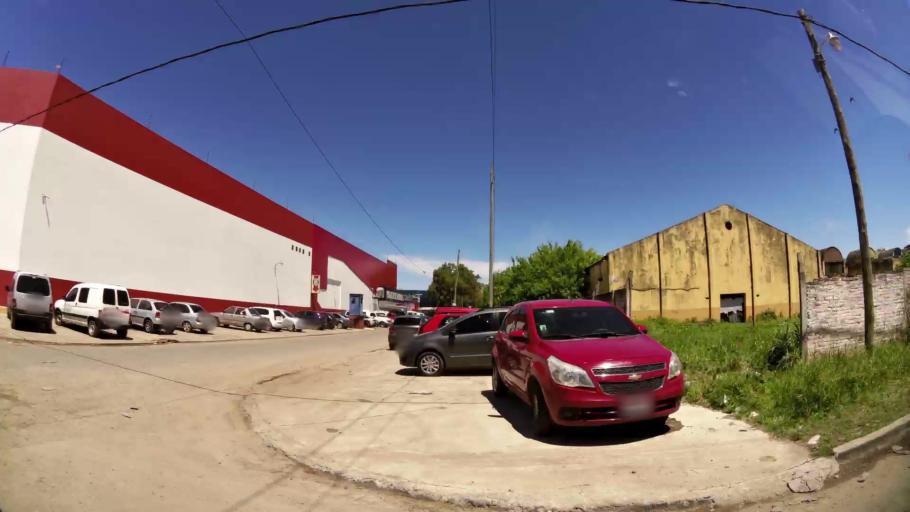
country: AR
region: Buenos Aires
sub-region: Partido de Quilmes
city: Quilmes
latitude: -34.7359
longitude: -58.2933
